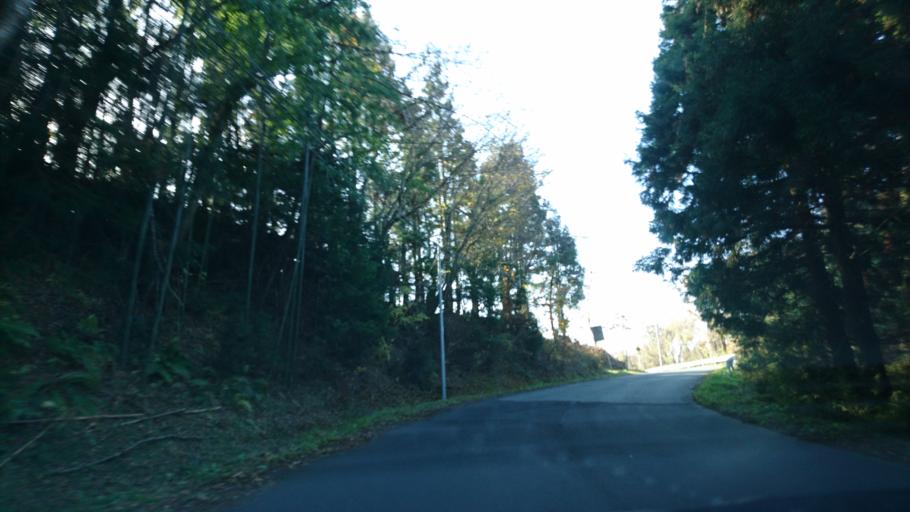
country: JP
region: Iwate
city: Ichinoseki
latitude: 38.8729
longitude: 141.3011
